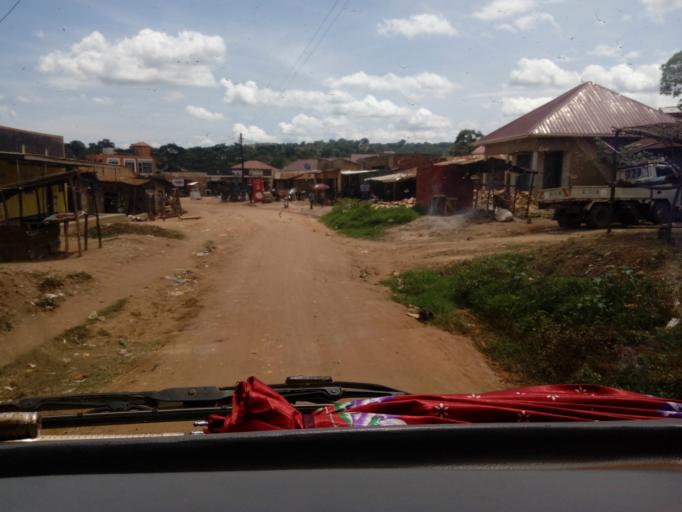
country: UG
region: Central Region
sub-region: Mubende District
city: Mubende
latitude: 0.4484
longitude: 31.6888
